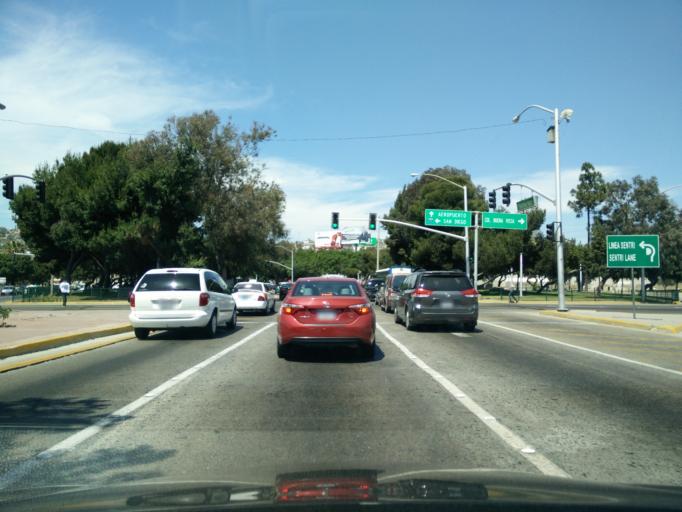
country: MX
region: Baja California
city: Tijuana
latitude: 32.5290
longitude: -117.0138
